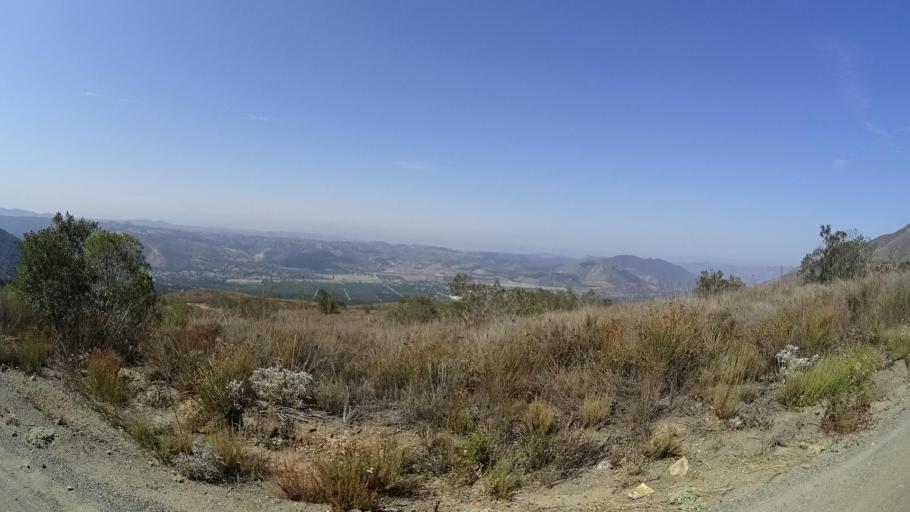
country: US
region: California
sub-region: San Diego County
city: Valley Center
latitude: 33.3309
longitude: -116.9590
